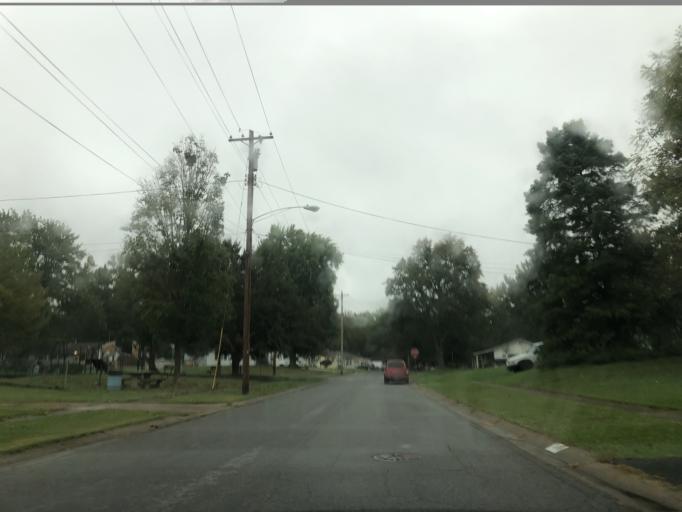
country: US
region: Ohio
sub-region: Hamilton County
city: Loveland
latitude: 39.2674
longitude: -84.2771
